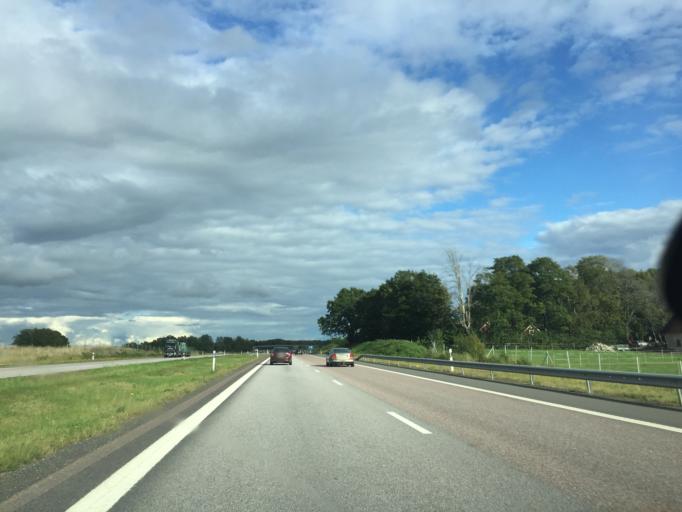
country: SE
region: OErebro
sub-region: Orebro Kommun
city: Hovsta
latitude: 59.3070
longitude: 15.3559
